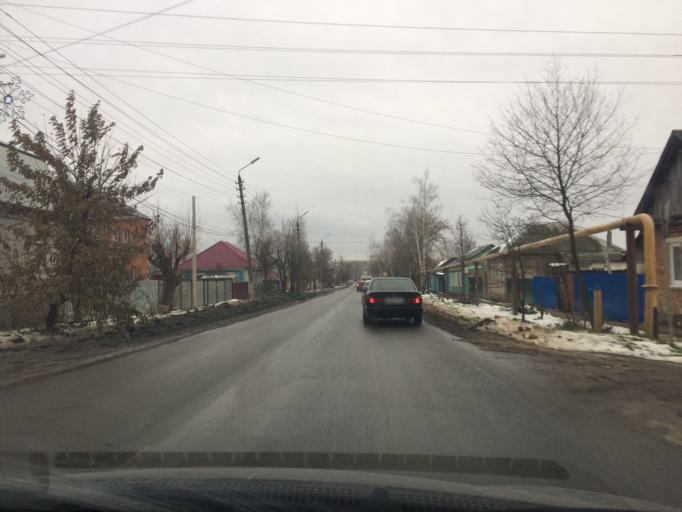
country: RU
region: Tula
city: Gorelki
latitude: 54.2391
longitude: 37.6395
